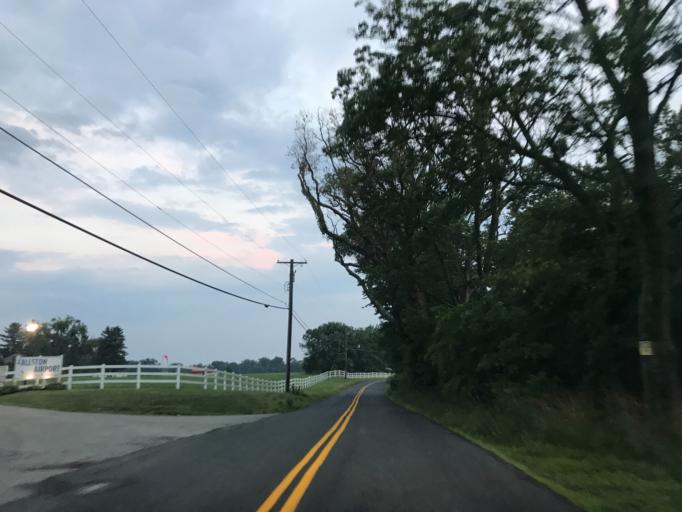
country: US
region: Maryland
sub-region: Harford County
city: Fallston
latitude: 39.5047
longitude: -76.4112
